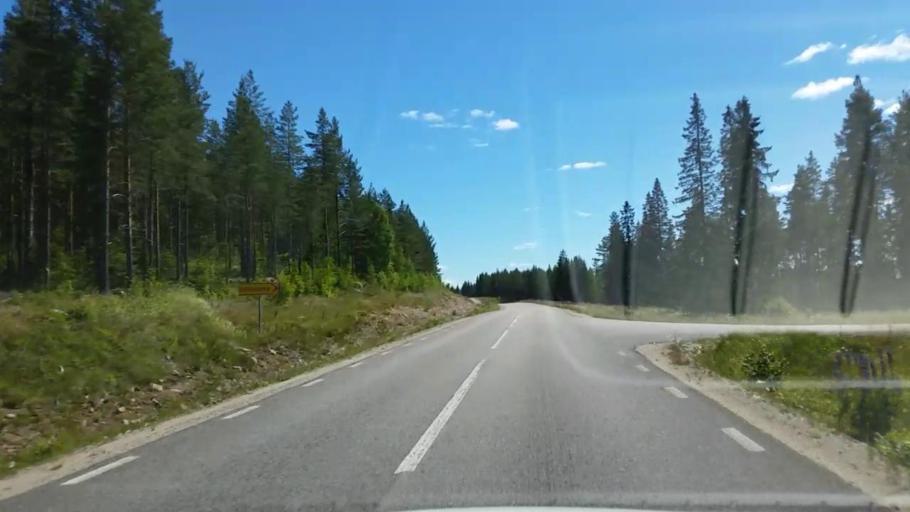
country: SE
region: Gaevleborg
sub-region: Ovanakers Kommun
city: Edsbyn
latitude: 61.6021
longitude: 15.5491
